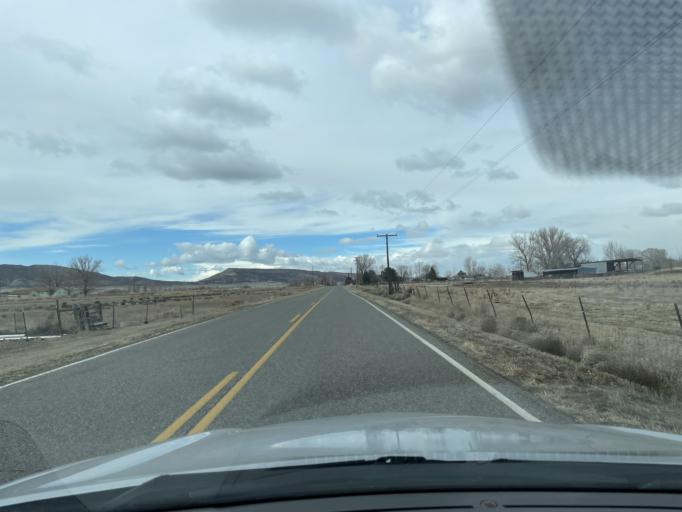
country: US
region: Colorado
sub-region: Mesa County
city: Loma
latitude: 39.2078
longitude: -108.8097
